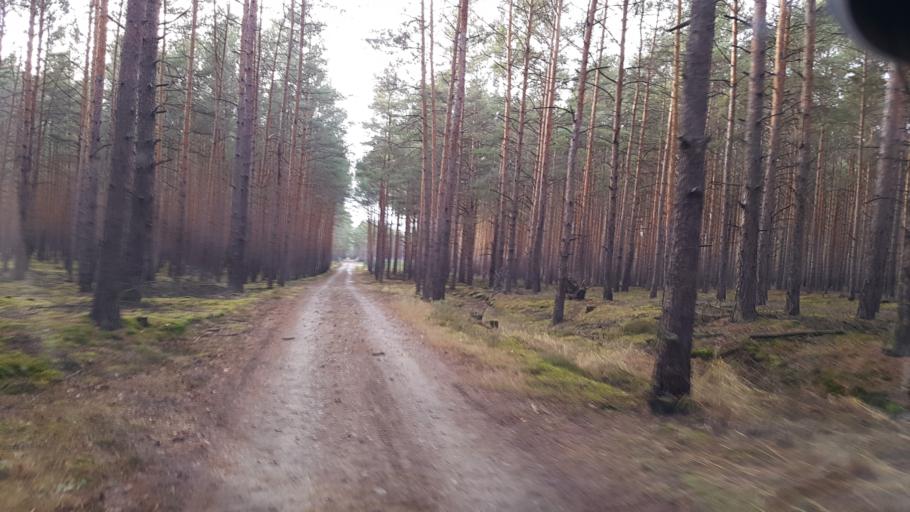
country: DE
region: Brandenburg
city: Sallgast
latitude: 51.6350
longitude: 13.8401
